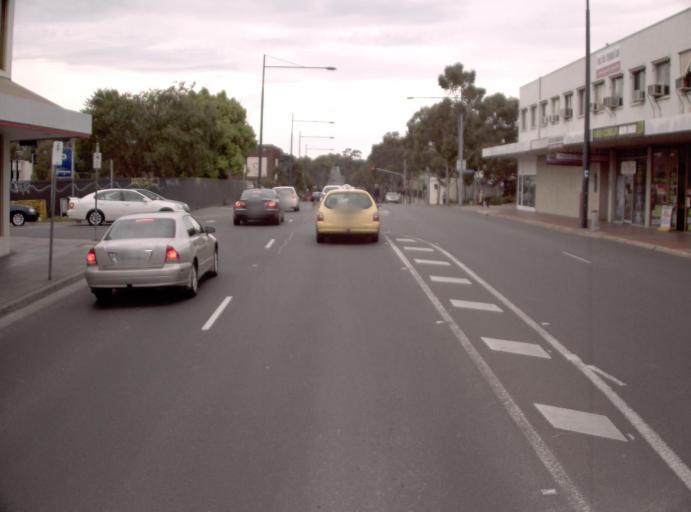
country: AU
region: Victoria
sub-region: Maroondah
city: Ringwood East
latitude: -37.8153
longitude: 145.2273
